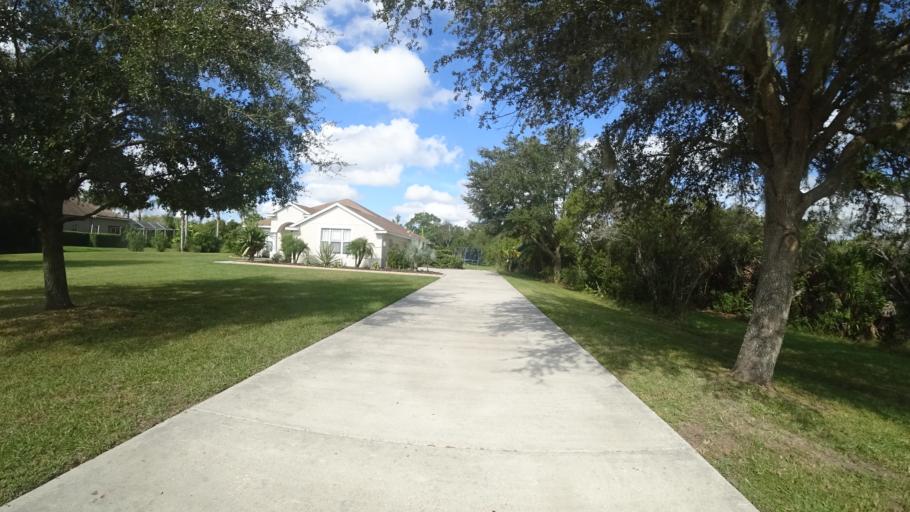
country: US
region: Florida
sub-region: Sarasota County
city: Fruitville
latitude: 27.3944
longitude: -82.3028
